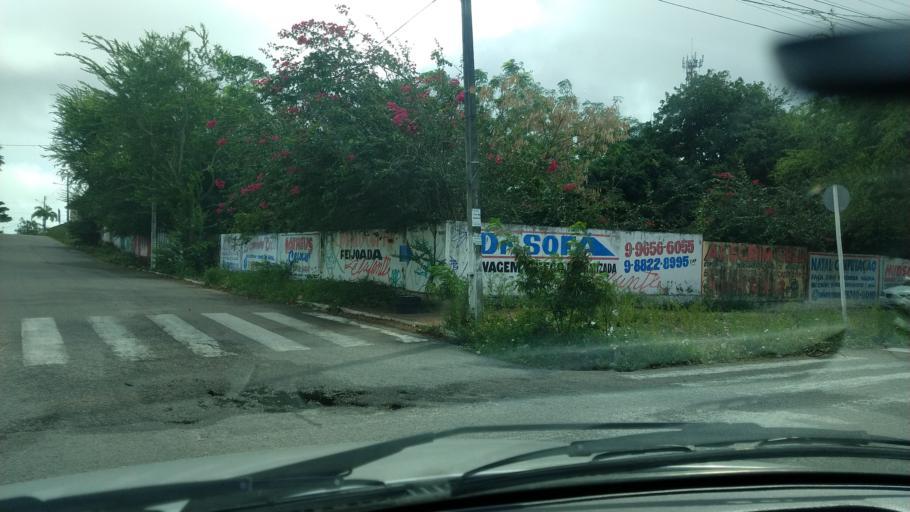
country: BR
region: Rio Grande do Norte
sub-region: Natal
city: Natal
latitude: -5.8188
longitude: -35.2214
